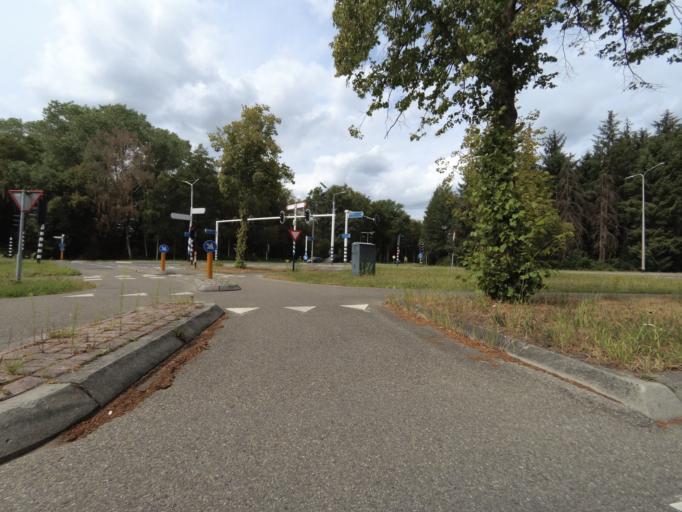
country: NL
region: Overijssel
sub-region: Gemeente Enschede
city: Enschede
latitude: 52.2405
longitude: 6.9173
